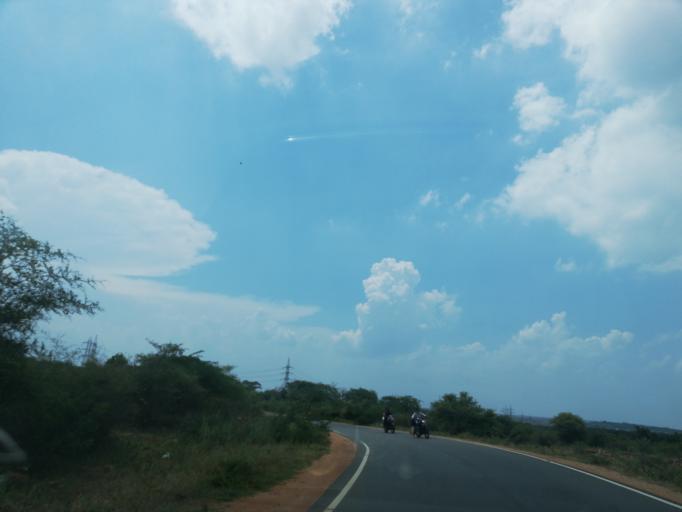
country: IN
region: Andhra Pradesh
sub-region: Guntur
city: Macherla
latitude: 16.5684
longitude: 79.3441
